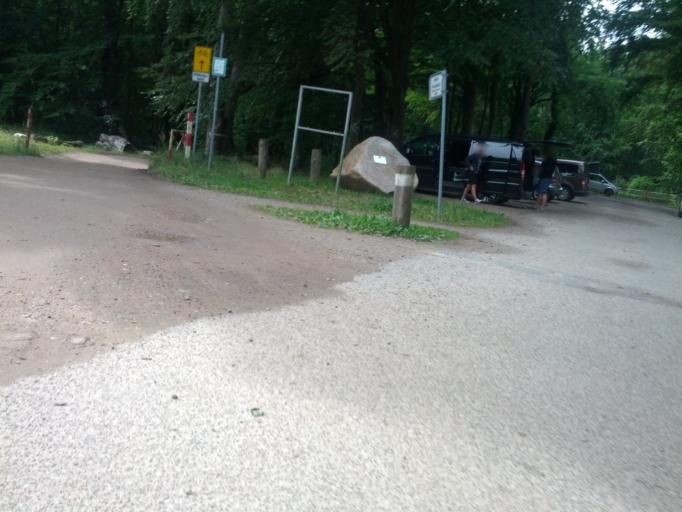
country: DE
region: Mecklenburg-Vorpommern
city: Ostseebad Kuhlungsborn
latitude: 54.1444
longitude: 11.8261
